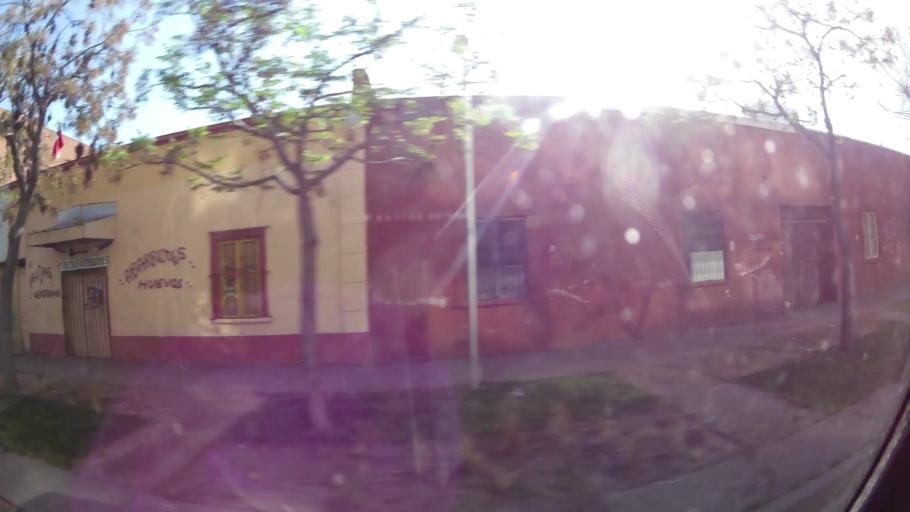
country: CL
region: Santiago Metropolitan
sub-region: Provincia de Santiago
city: Santiago
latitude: -33.4283
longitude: -70.6754
